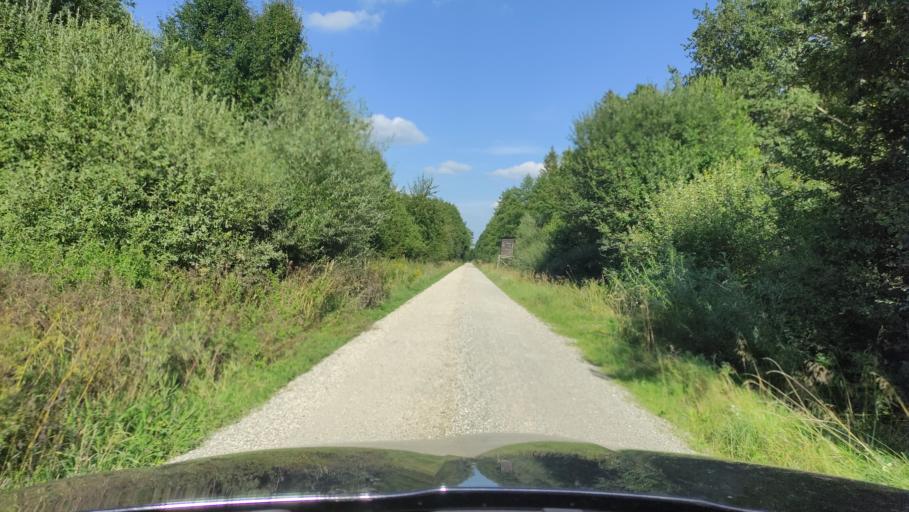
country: DE
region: Bavaria
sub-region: Swabia
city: Breitenthal
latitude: 48.2824
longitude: 10.2825
